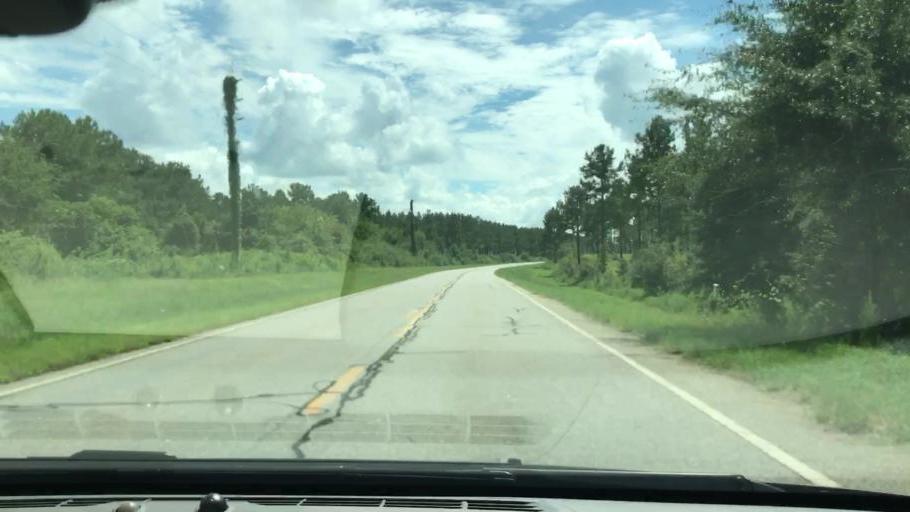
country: US
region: Georgia
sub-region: Quitman County
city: Georgetown
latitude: 32.0720
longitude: -85.0370
